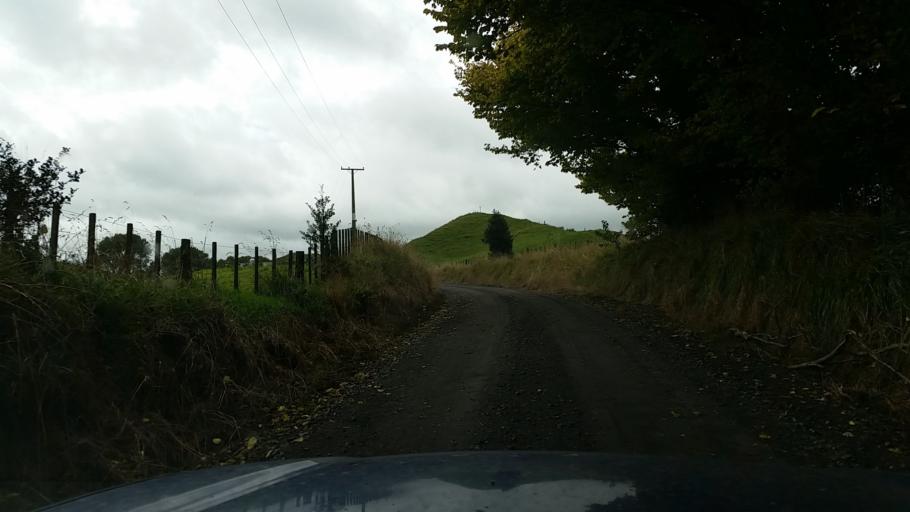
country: NZ
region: Taranaki
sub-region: South Taranaki District
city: Eltham
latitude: -39.3546
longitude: 174.4349
